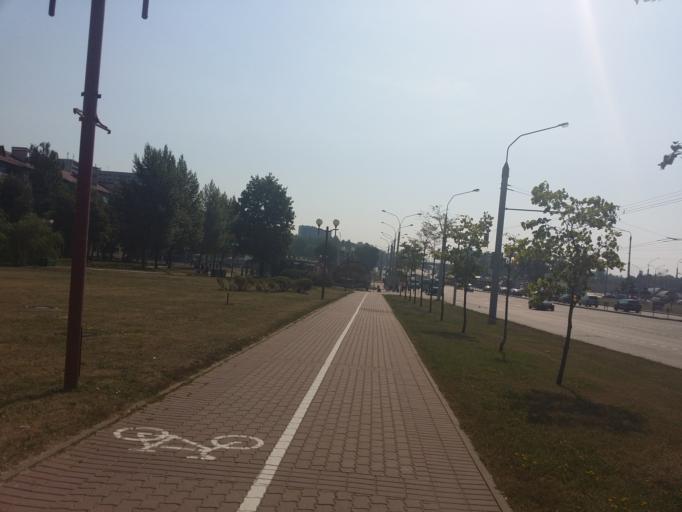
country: BY
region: Minsk
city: Vyaliki Trastsyanets
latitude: 53.8628
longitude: 27.6718
